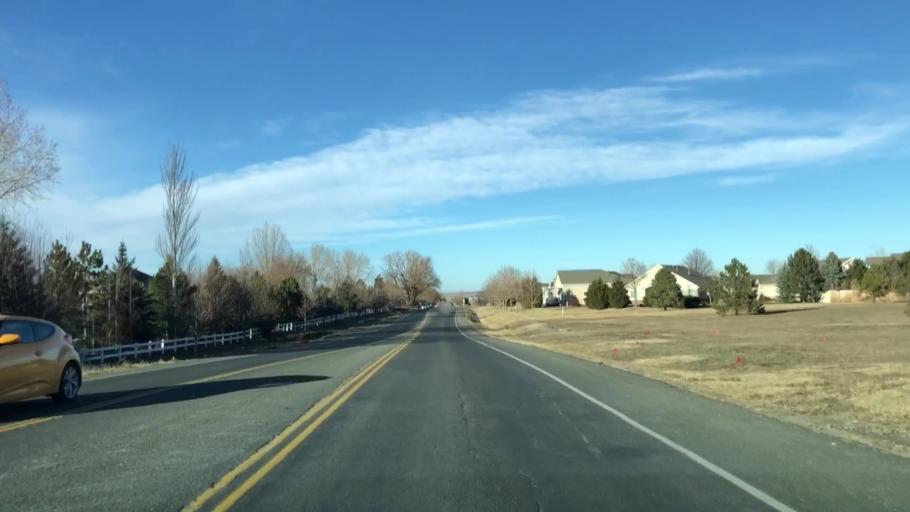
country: US
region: Colorado
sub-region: Weld County
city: Windsor
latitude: 40.4676
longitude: -104.9822
